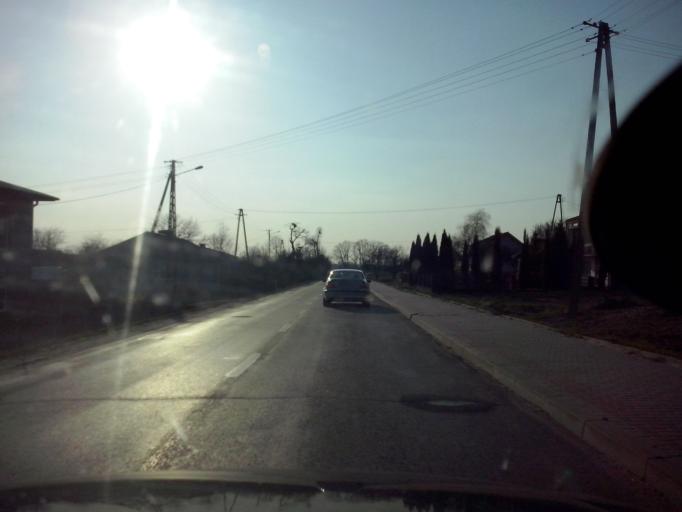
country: PL
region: Lublin Voivodeship
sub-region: Powiat janowski
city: Modliborzyce
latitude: 50.7552
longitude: 22.3040
